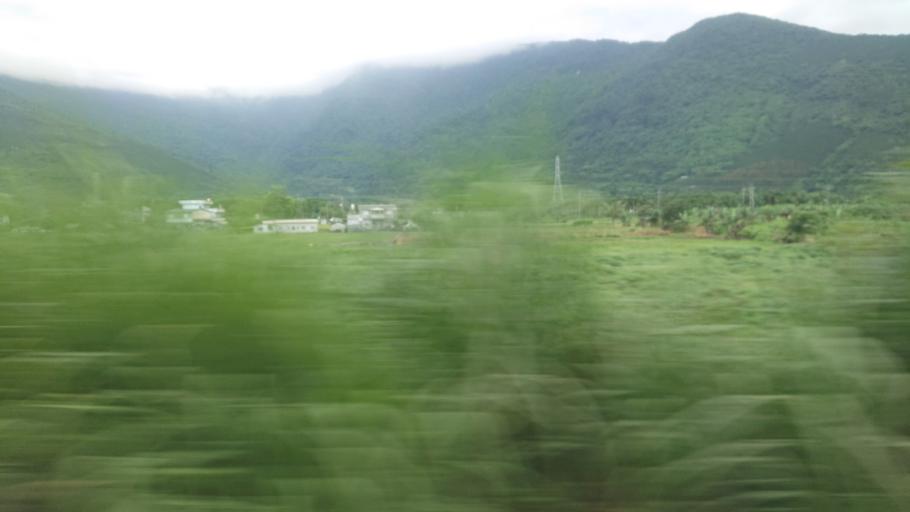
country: TW
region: Taiwan
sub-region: Hualien
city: Hualian
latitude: 23.7513
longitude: 121.4492
